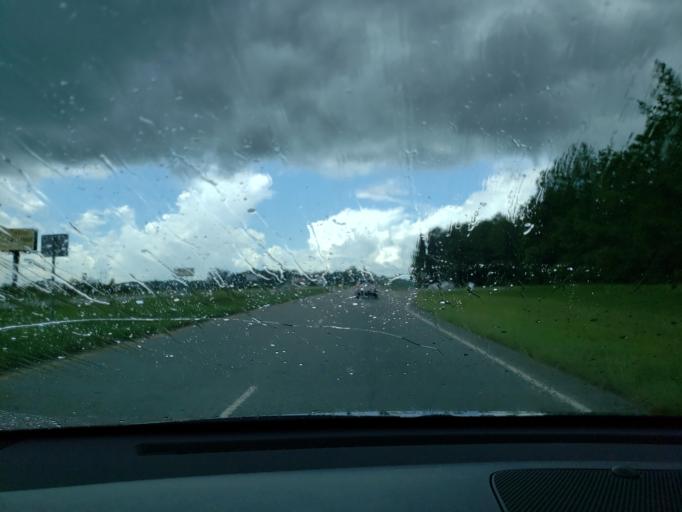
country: US
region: North Carolina
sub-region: Bladen County
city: Elizabethtown
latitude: 34.6048
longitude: -78.6257
